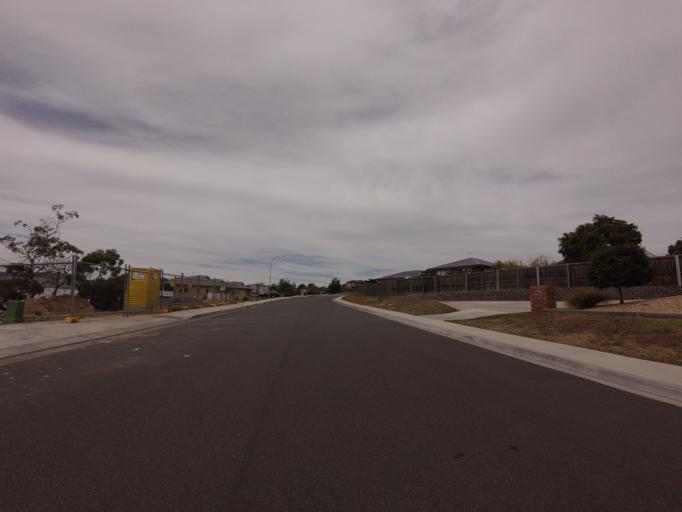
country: AU
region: Tasmania
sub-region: Sorell
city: Sorell
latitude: -42.7923
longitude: 147.5309
